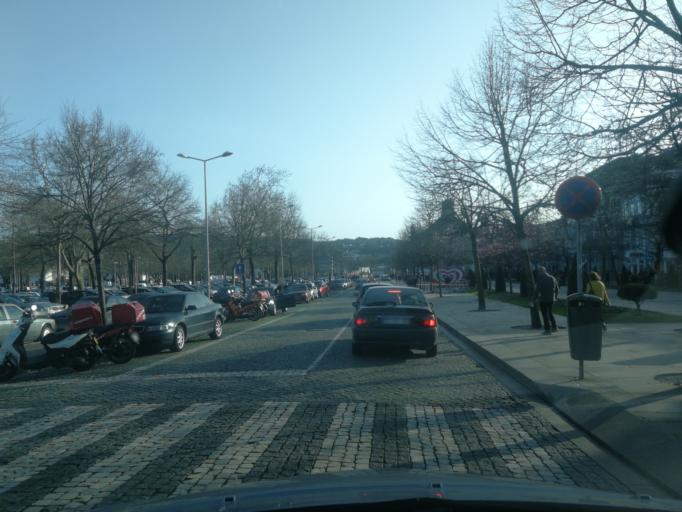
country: PT
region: Braga
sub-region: Barcelos
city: Barcelos
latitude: 41.5335
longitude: -8.6193
